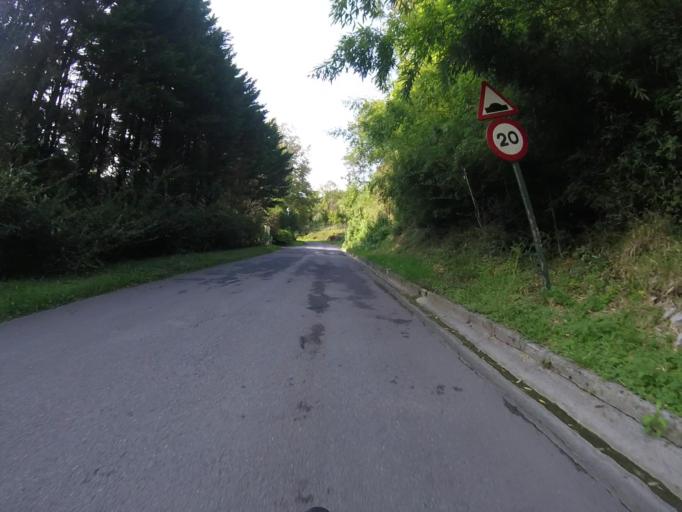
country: ES
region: Basque Country
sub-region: Provincia de Guipuzcoa
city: Irun
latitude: 43.3359
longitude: -1.8321
